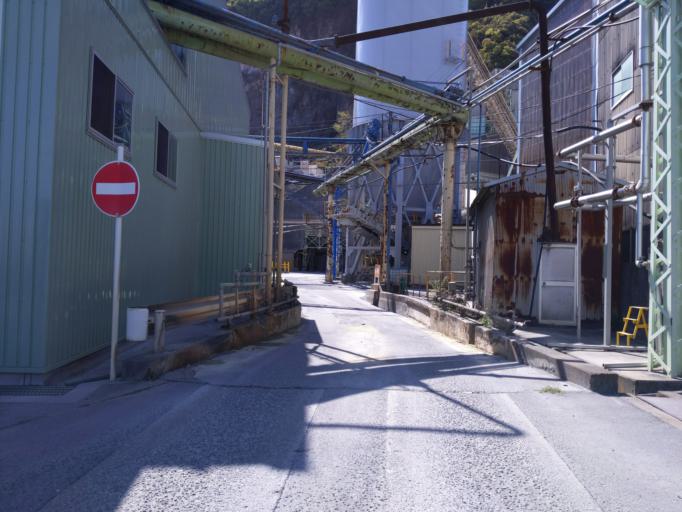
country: JP
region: Gifu
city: Godo
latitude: 35.3981
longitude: 136.5817
